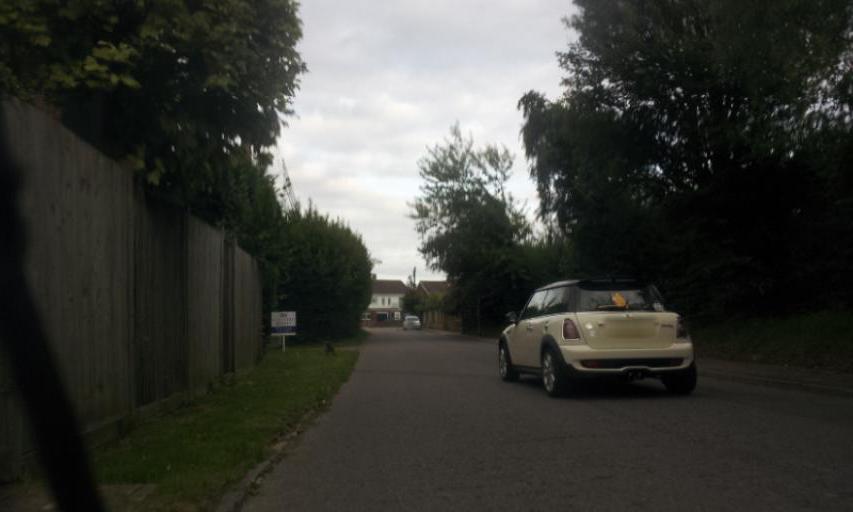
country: GB
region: England
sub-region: Kent
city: East Peckham
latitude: 51.2180
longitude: 0.3923
